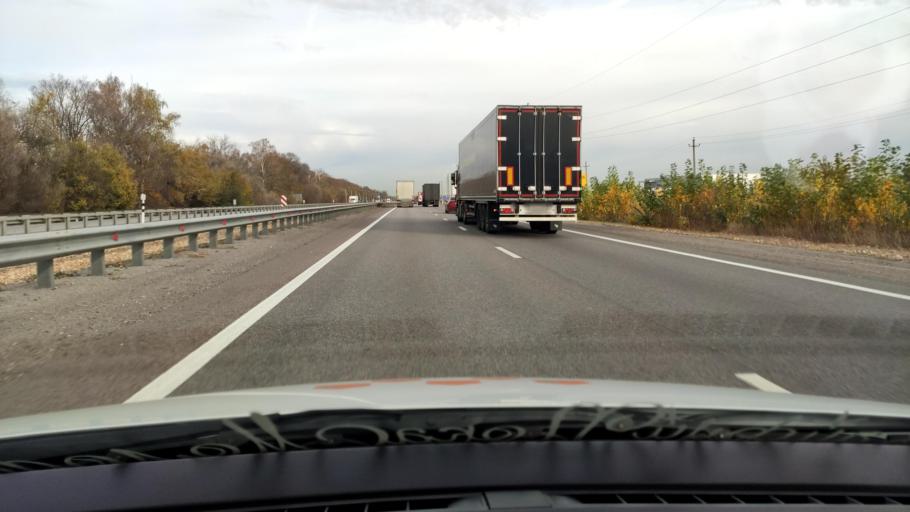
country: RU
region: Voronezj
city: Ramon'
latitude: 51.9015
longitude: 39.2188
